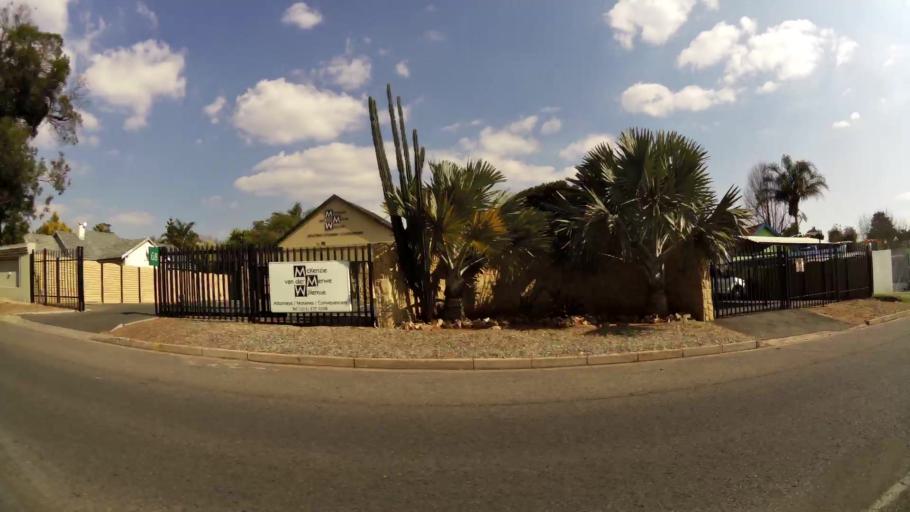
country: ZA
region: Gauteng
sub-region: City of Johannesburg Metropolitan Municipality
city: Modderfontein
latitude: -26.0907
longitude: 28.2501
